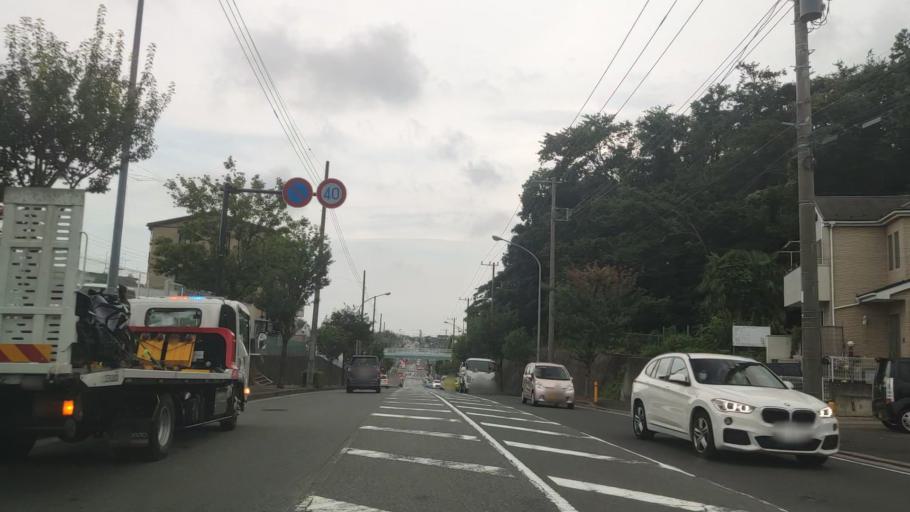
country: JP
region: Kanagawa
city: Minami-rinkan
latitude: 35.4556
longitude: 139.4818
